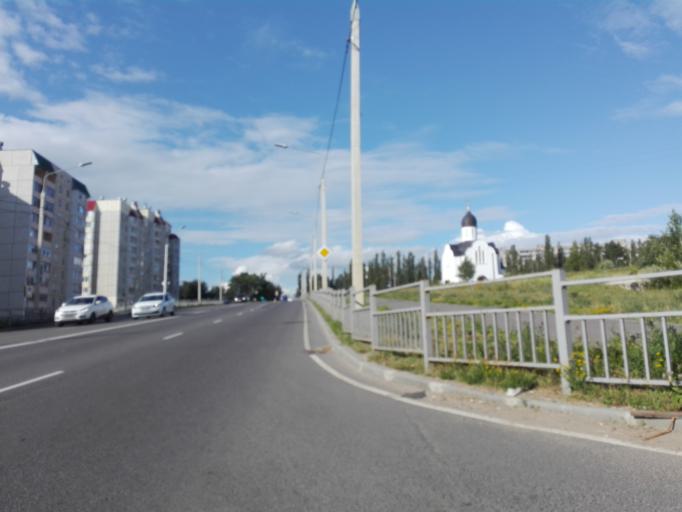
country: RU
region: Orjol
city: Orel
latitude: 53.0155
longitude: 36.1334
